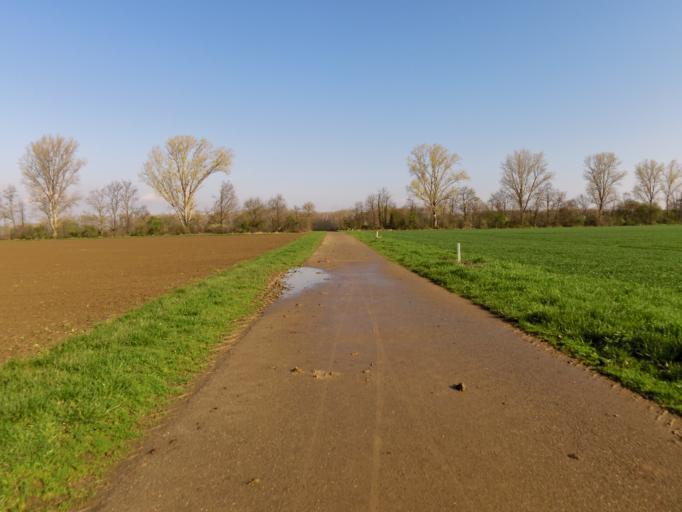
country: DE
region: Rheinland-Pfalz
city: Bobenheim-Roxheim
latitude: 49.5978
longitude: 8.3941
